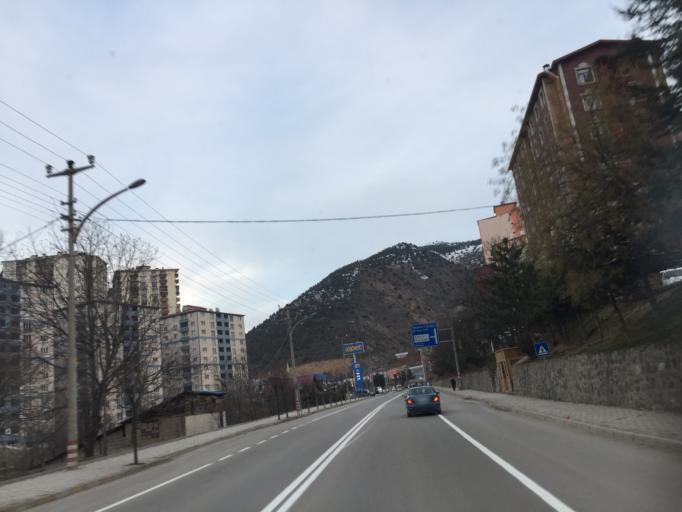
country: TR
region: Gumushane
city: Gumushkhane
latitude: 40.4644
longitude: 39.4646
